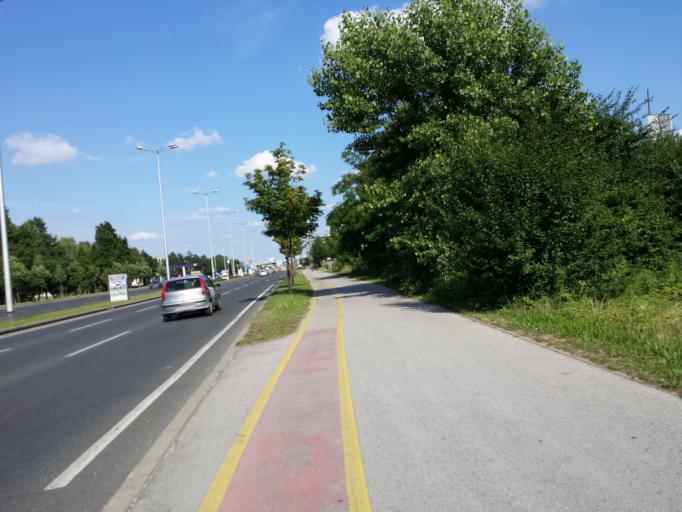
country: HR
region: Grad Zagreb
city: Jankomir
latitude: 45.7956
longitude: 15.9149
